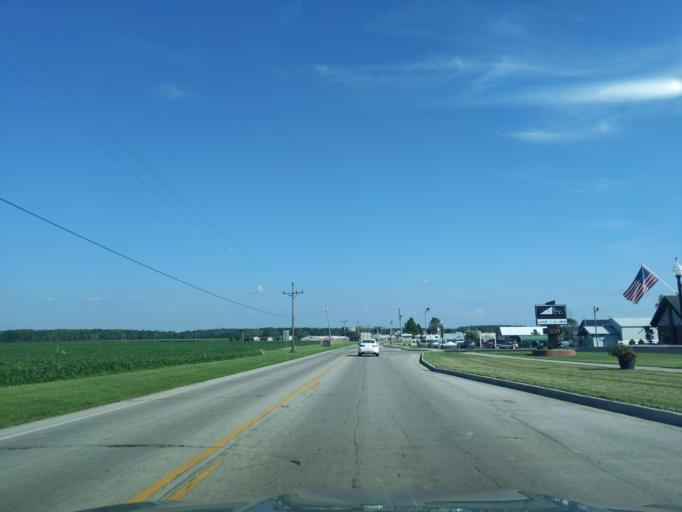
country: US
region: Indiana
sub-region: Ripley County
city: Osgood
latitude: 39.1214
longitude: -85.2859
